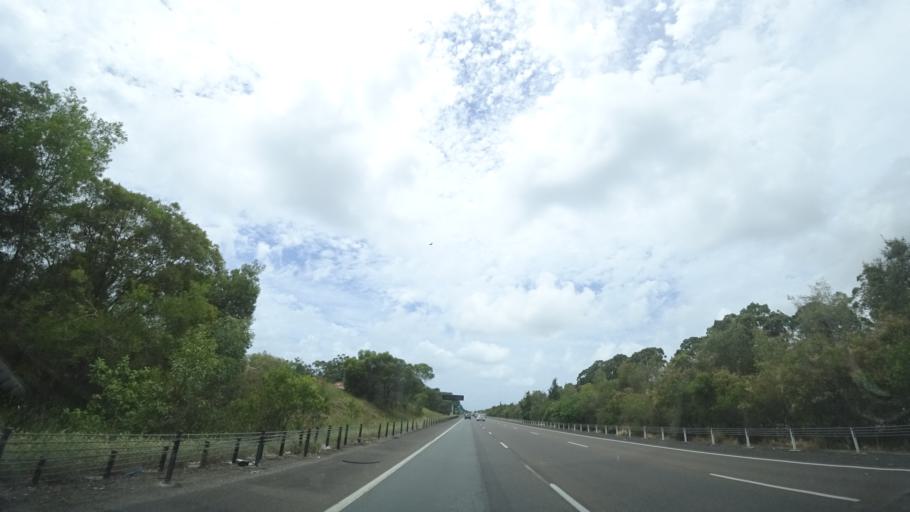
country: AU
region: Queensland
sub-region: Sunshine Coast
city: Mooloolaba
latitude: -26.6806
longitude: 153.1014
